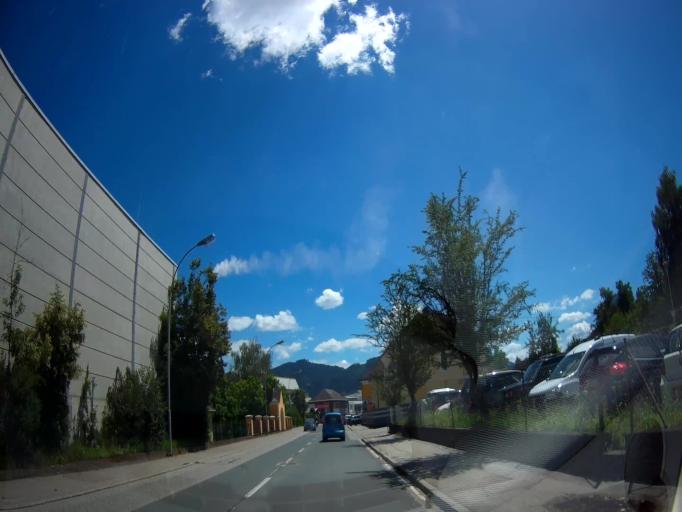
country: AT
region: Carinthia
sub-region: Politischer Bezirk Sankt Veit an der Glan
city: Sankt Veit an der Glan
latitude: 46.7585
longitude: 14.3755
